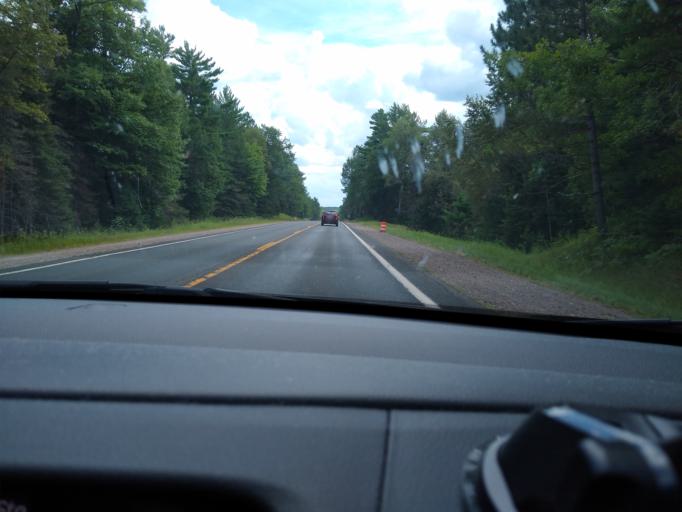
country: US
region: Michigan
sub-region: Iron County
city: Crystal Falls
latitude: 46.2544
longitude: -88.0121
